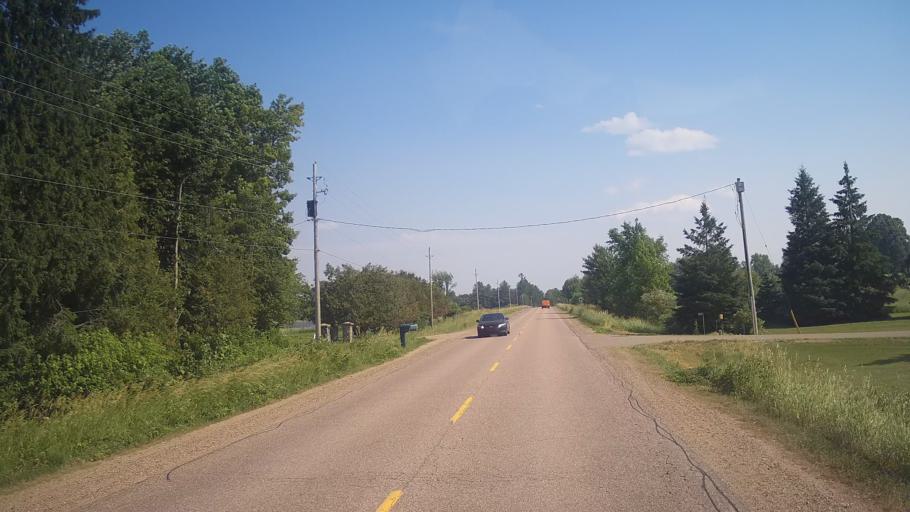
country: CA
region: Ontario
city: Pembroke
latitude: 45.5924
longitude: -77.2287
